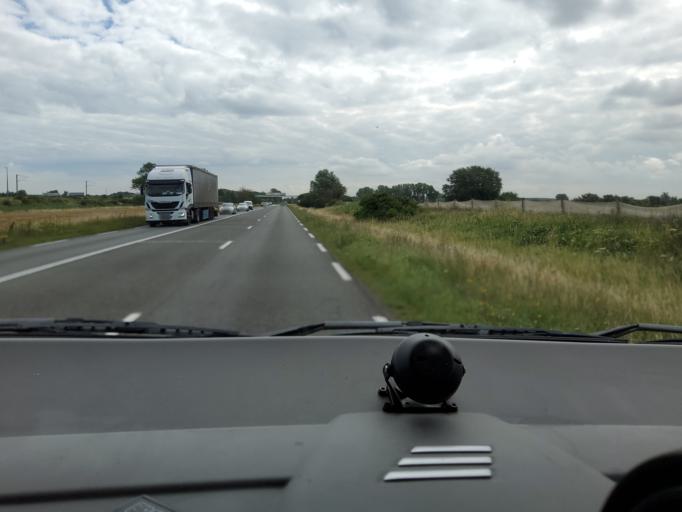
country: FR
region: Nord-Pas-de-Calais
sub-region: Departement du Nord
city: Loon-Plage
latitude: 50.9957
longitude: 2.1888
